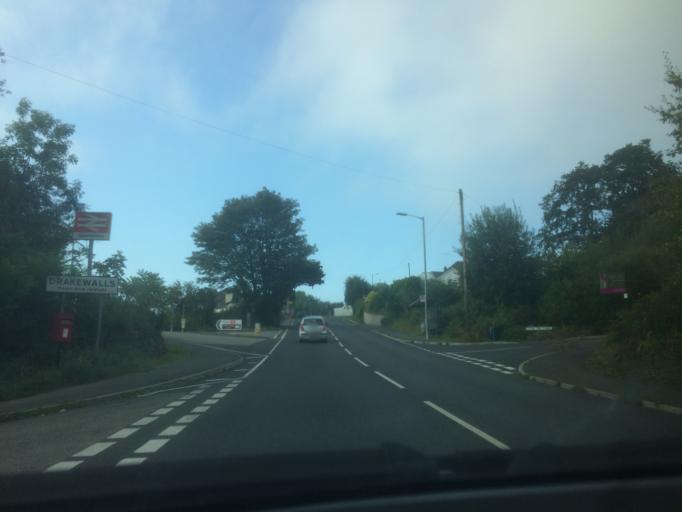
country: GB
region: England
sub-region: Cornwall
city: Gunnislake
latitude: 50.5172
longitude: -4.2196
